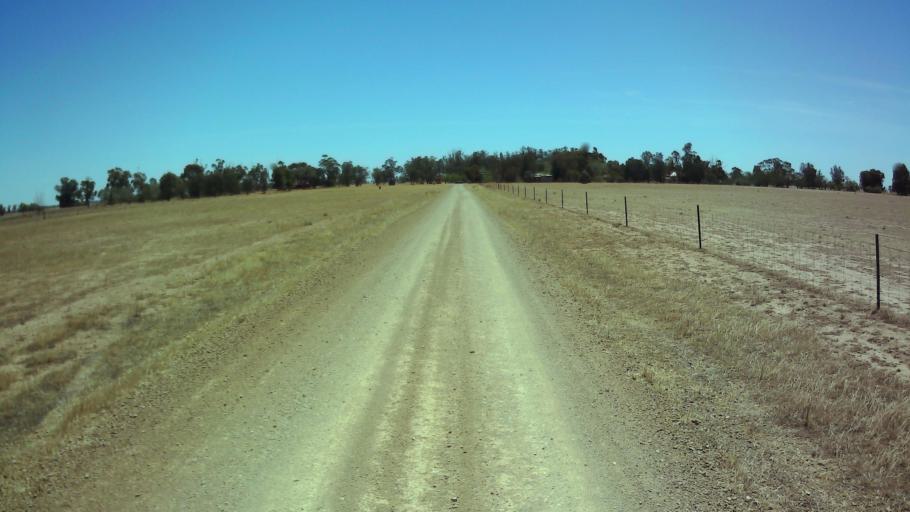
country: AU
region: New South Wales
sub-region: Weddin
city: Grenfell
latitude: -33.9973
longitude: 147.7353
